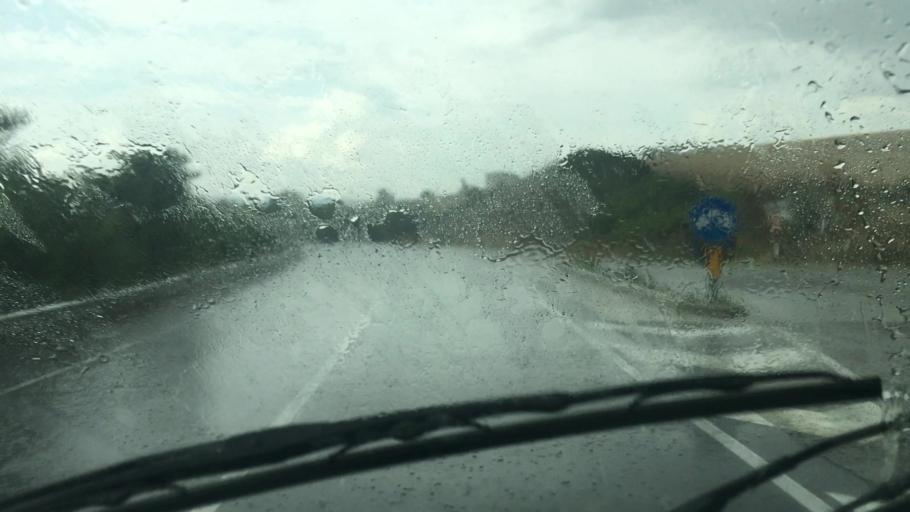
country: IT
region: Basilicate
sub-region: Provincia di Matera
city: Matera
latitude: 40.6235
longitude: 16.5858
